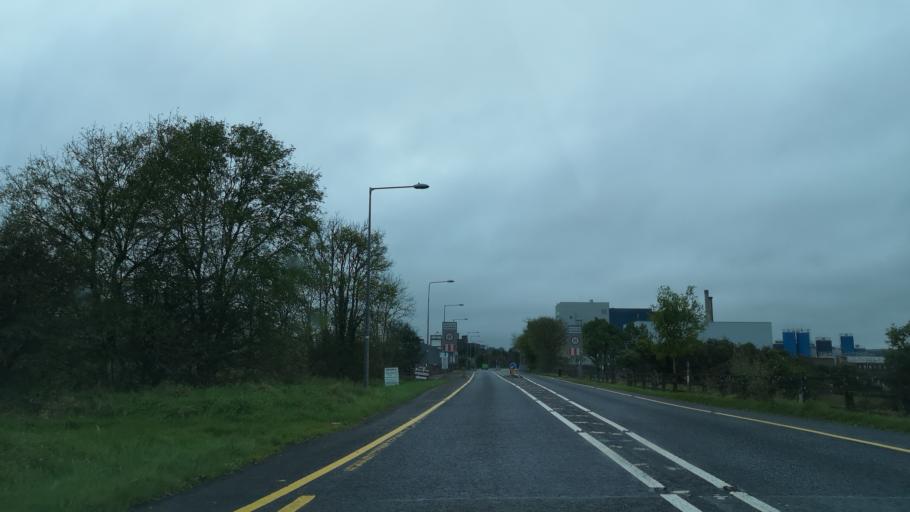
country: IE
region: Connaught
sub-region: Roscommon
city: Ballaghaderreen
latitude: 53.8965
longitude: -8.5646
